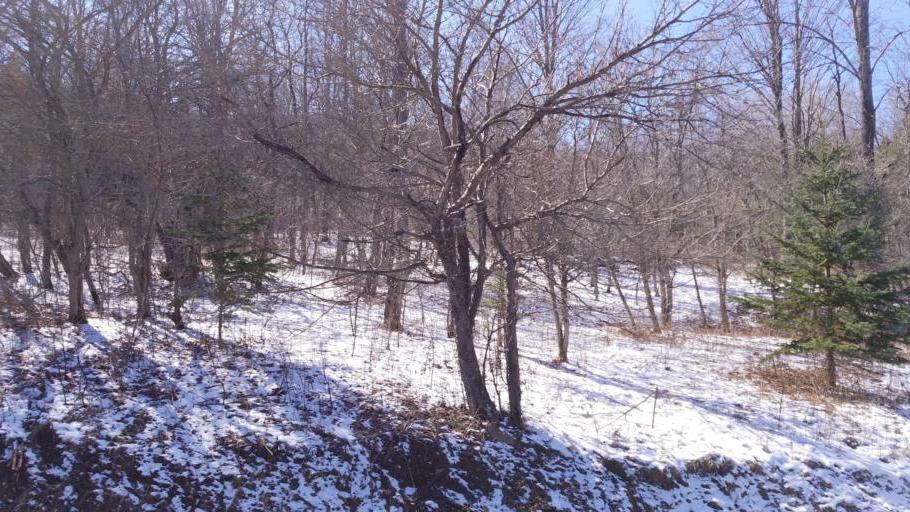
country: US
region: New York
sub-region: Allegany County
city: Andover
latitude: 41.9519
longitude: -77.8289
